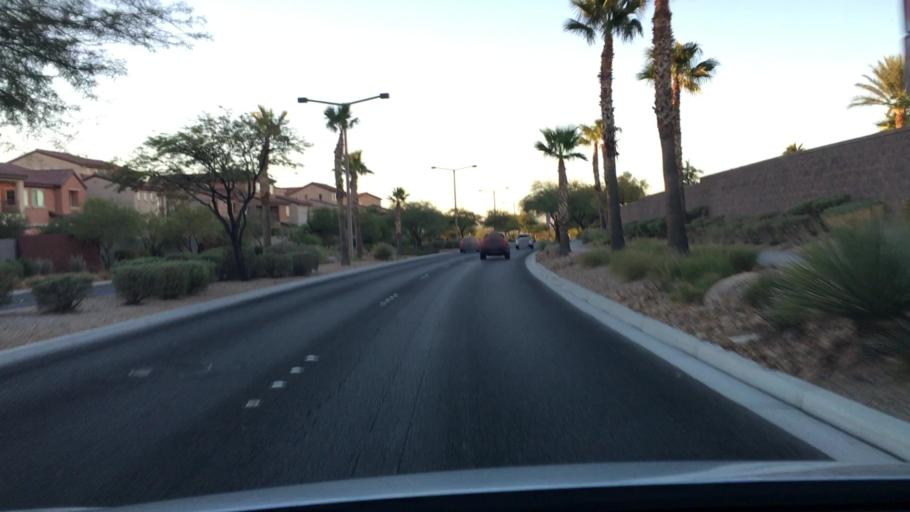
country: US
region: Nevada
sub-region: Clark County
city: Summerlin South
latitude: 36.1521
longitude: -115.3434
